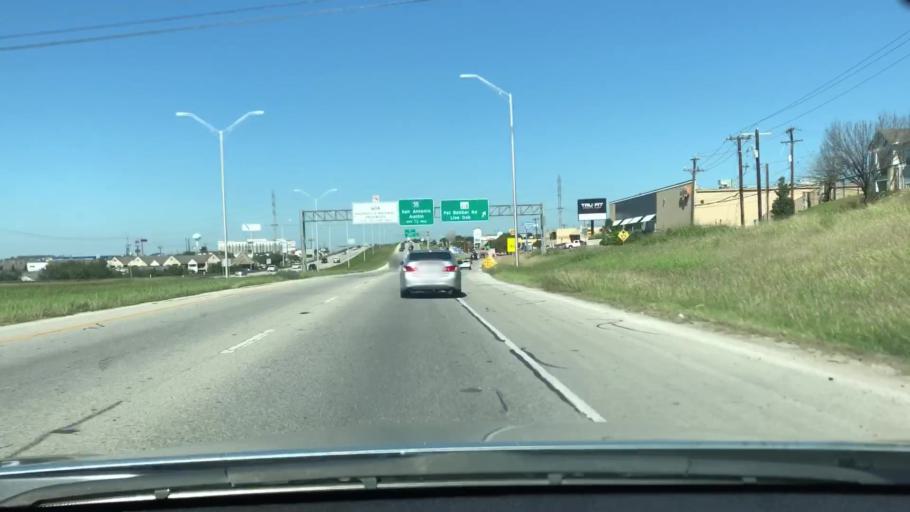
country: US
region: Texas
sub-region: Bexar County
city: Live Oak
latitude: 29.5560
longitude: -98.3240
